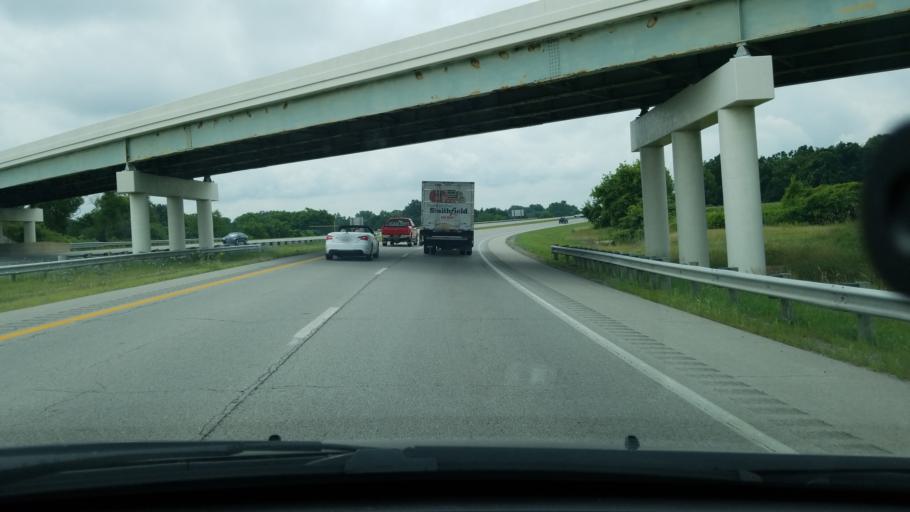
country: US
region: Ohio
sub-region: Erie County
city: Huron
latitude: 41.3981
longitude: -82.5755
